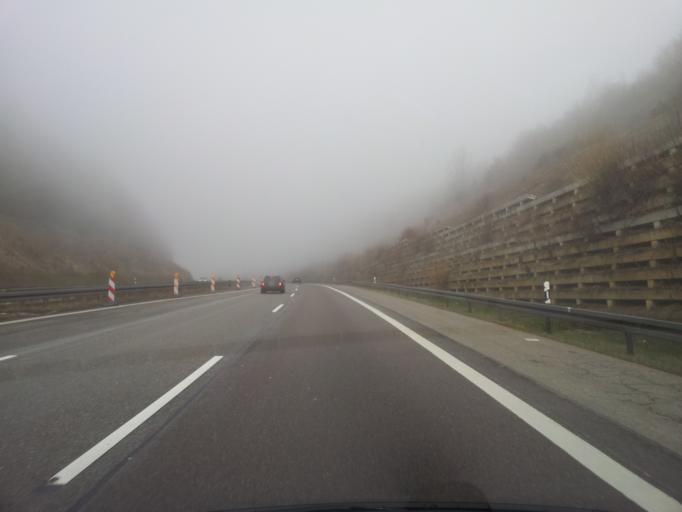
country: DE
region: Baden-Wuerttemberg
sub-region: Freiburg Region
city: Immendingen
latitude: 47.8902
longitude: 8.7293
